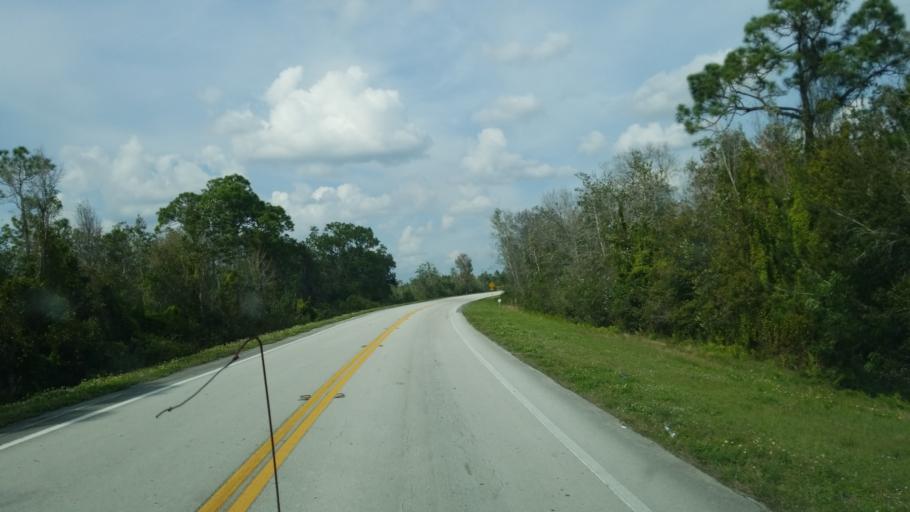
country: US
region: Florida
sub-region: Indian River County
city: Fellsmere
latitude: 27.7192
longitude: -80.9143
